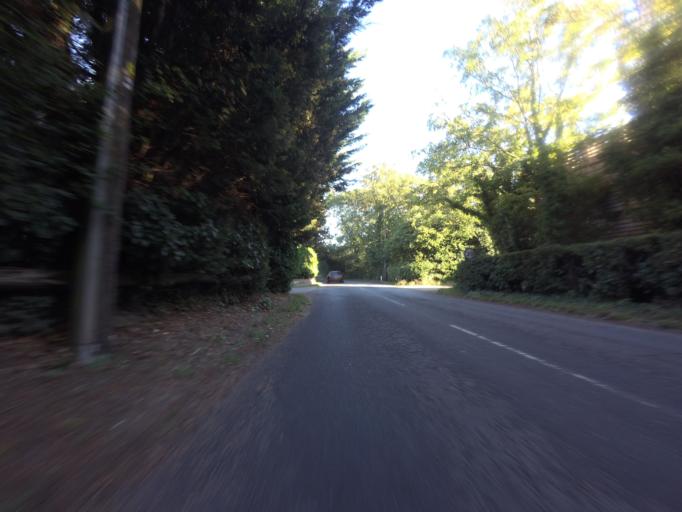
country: GB
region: England
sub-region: Kent
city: Herne Bay
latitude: 51.3438
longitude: 1.1883
